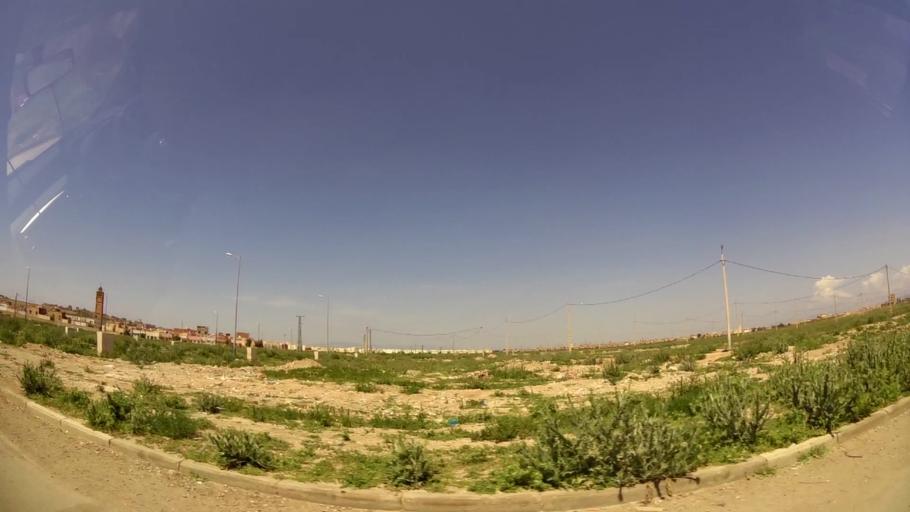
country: MA
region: Oriental
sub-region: Oujda-Angad
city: Oujda
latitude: 34.6924
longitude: -1.9370
